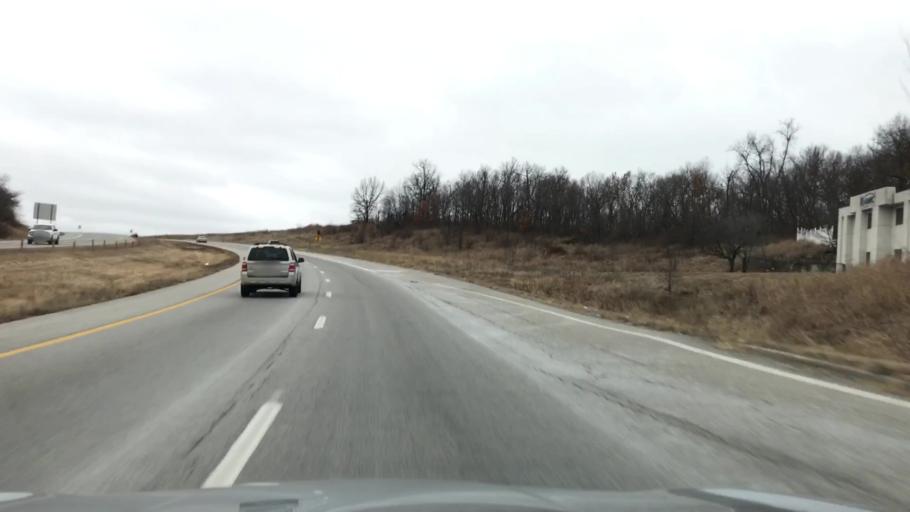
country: US
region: Missouri
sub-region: Jackson County
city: East Independence
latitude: 39.0572
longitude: -94.3672
